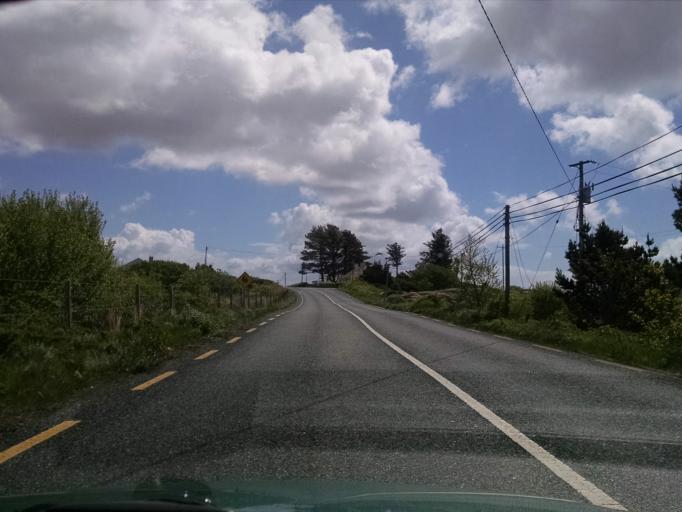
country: IE
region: Connaught
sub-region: County Galway
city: Oughterard
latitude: 53.3070
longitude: -9.5964
